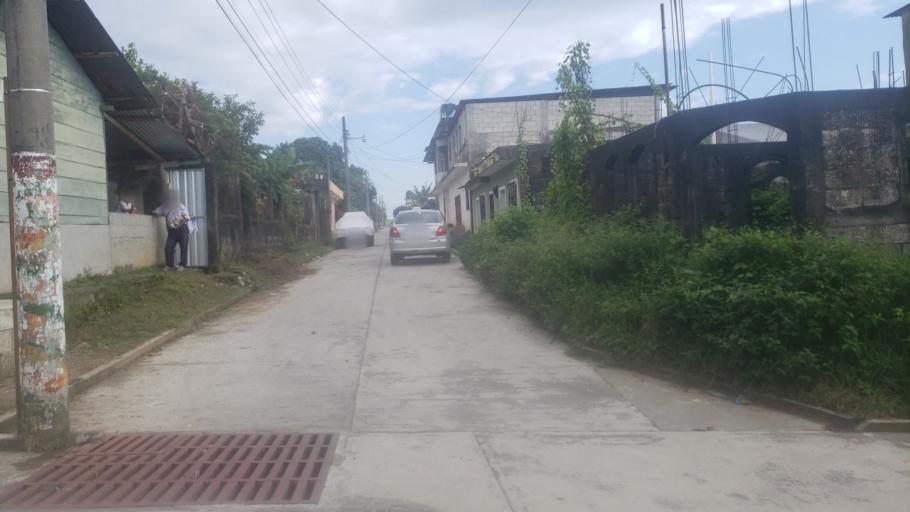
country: GT
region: Suchitepeque
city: Pueblo Nuevo
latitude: 14.6488
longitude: -91.5559
